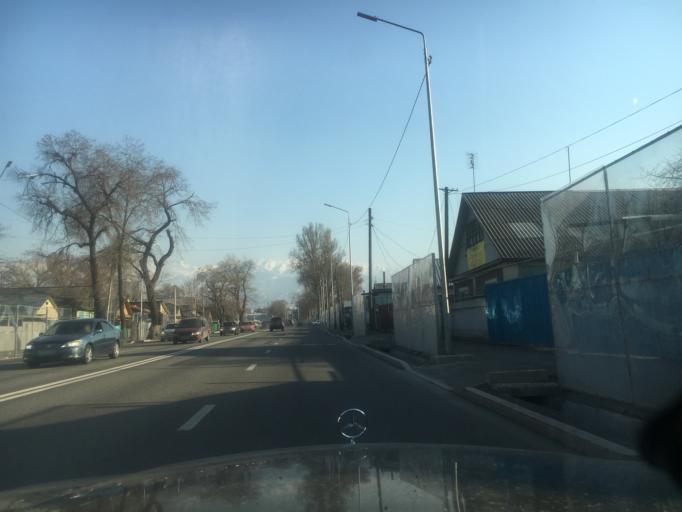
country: KZ
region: Almaty Qalasy
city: Almaty
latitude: 43.2815
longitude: 76.9394
